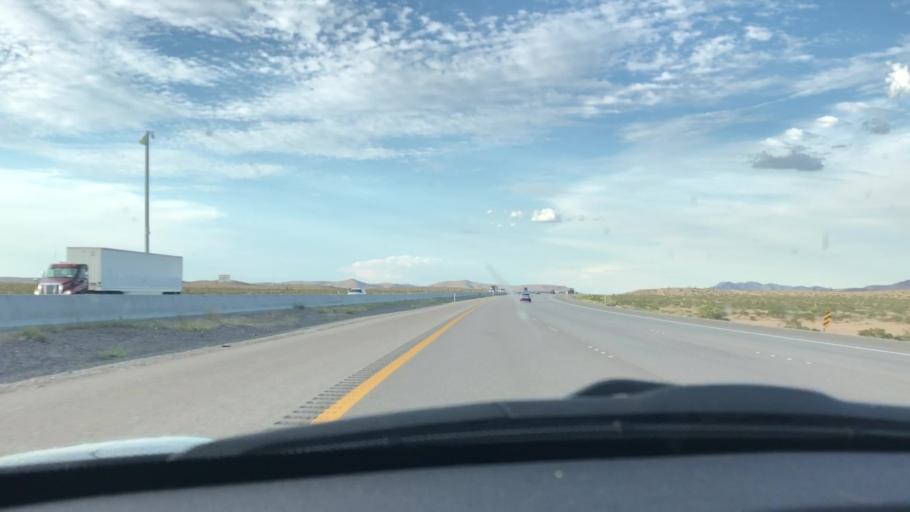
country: US
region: Nevada
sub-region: Clark County
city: Enterprise
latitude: 35.8229
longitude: -115.2973
